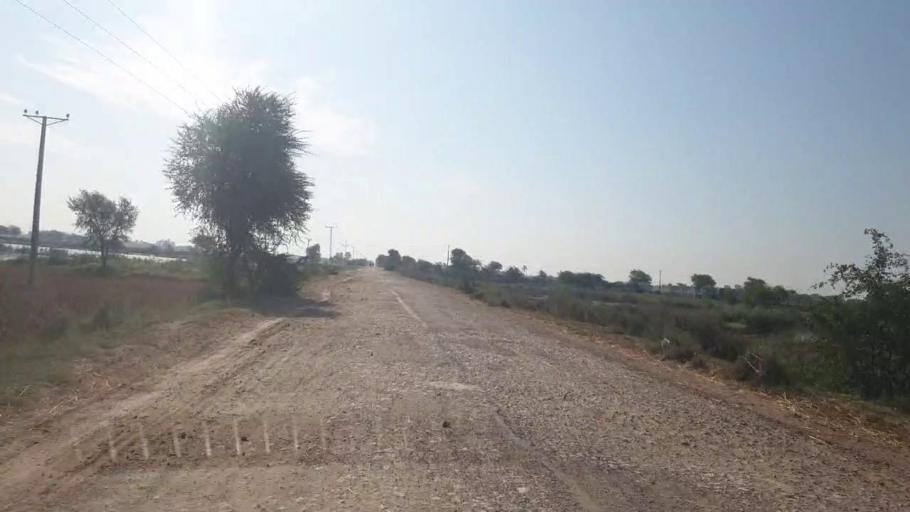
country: PK
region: Sindh
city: Talhar
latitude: 24.9117
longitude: 68.8185
